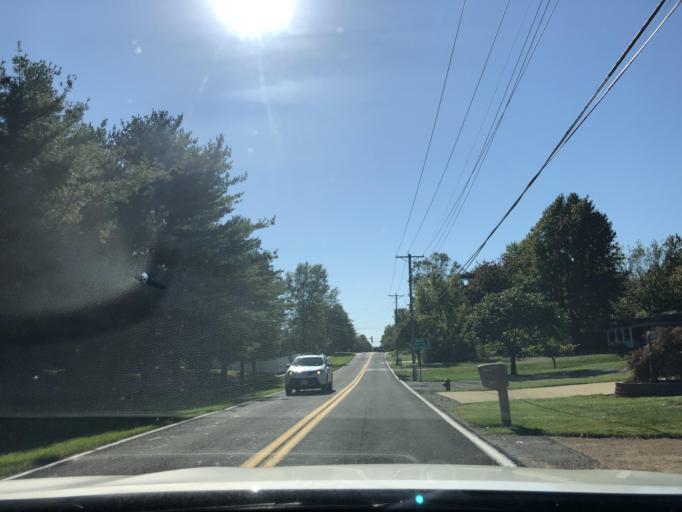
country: US
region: Missouri
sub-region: Saint Louis County
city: Concord
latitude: 38.4882
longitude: -90.3629
